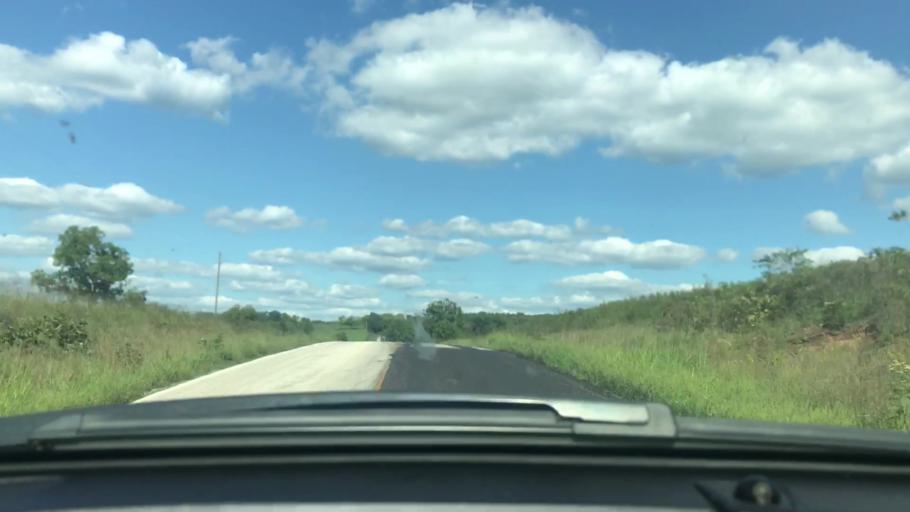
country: US
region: Missouri
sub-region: Wright County
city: Hartville
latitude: 37.3719
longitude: -92.3884
